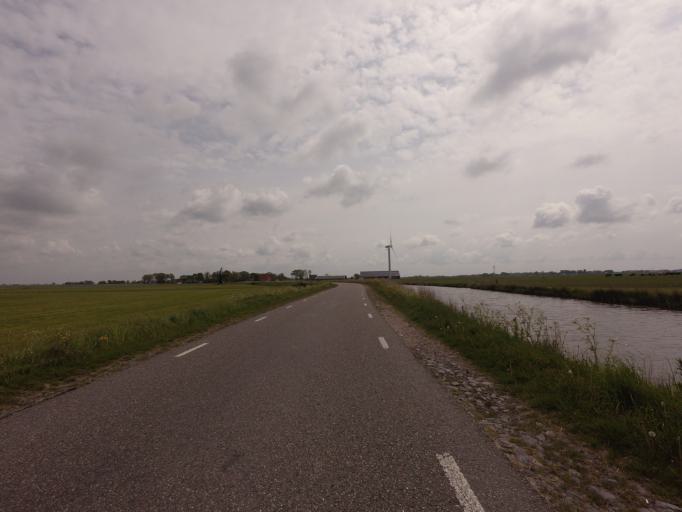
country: NL
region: Friesland
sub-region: Sudwest Fryslan
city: Bolsward
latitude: 53.1009
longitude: 5.5158
